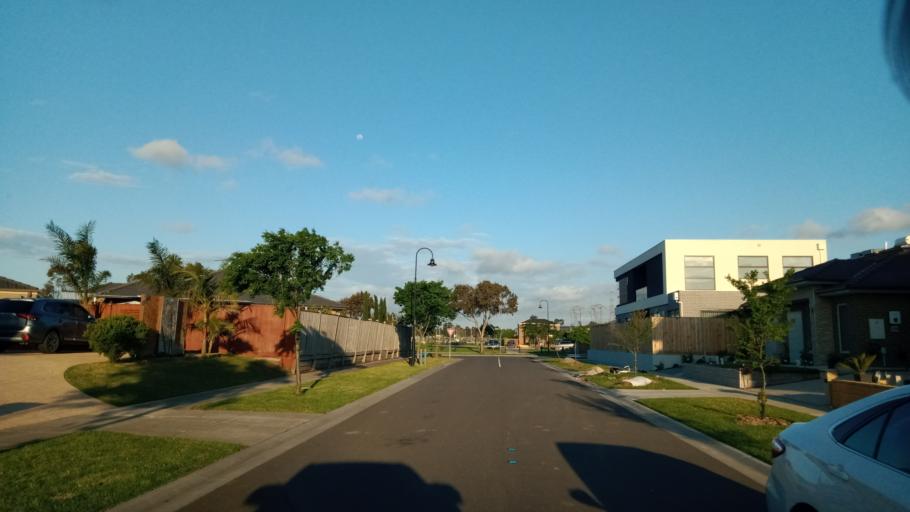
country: AU
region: Victoria
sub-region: Casey
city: Lynbrook
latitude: -38.0766
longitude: 145.2549
